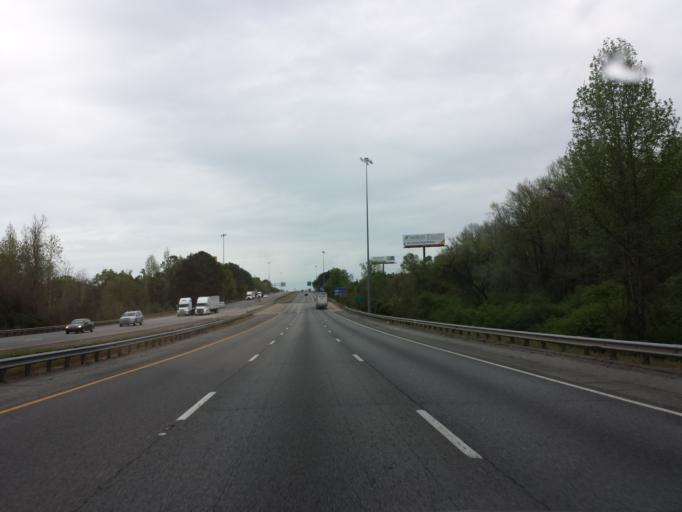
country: US
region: Georgia
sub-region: Houston County
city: Perry
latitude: 32.4568
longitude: -83.7512
